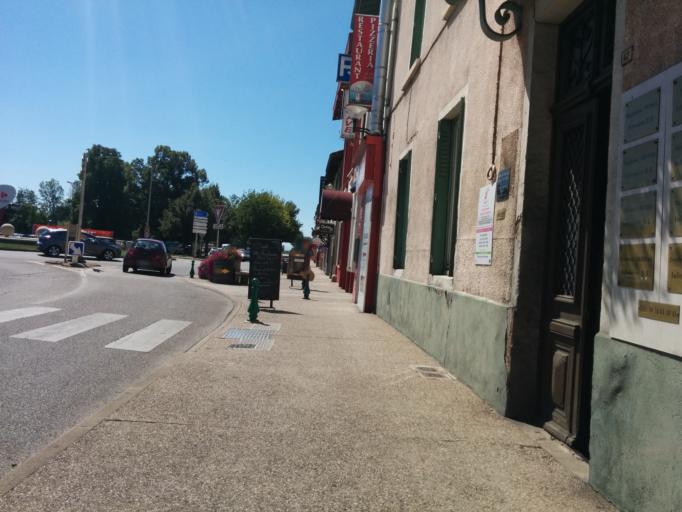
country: FR
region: Rhone-Alpes
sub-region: Departement de l'Ain
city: Meximieux
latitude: 45.9018
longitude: 5.1902
